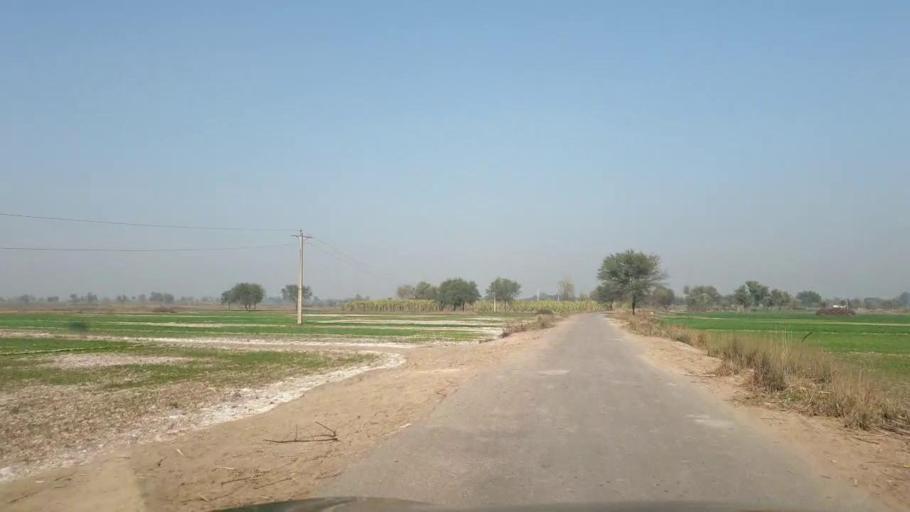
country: PK
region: Sindh
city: Ubauro
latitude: 28.1322
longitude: 69.7694
